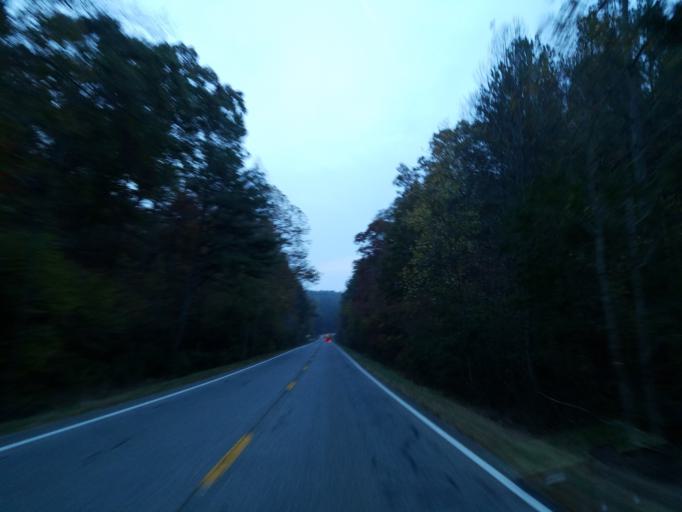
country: US
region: Georgia
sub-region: Pickens County
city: Jasper
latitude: 34.5349
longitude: -84.5743
